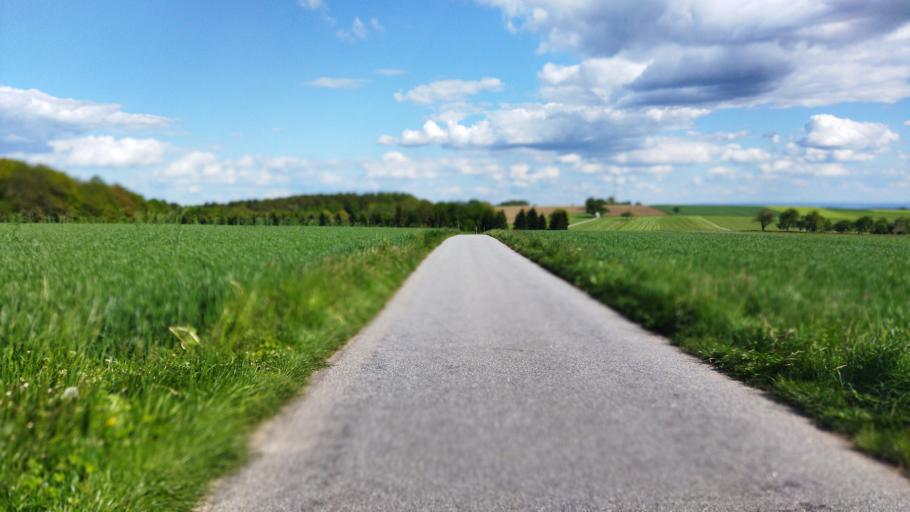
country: DE
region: Baden-Wuerttemberg
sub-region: Karlsruhe Region
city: Zwingenberg
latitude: 49.4488
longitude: 9.0661
